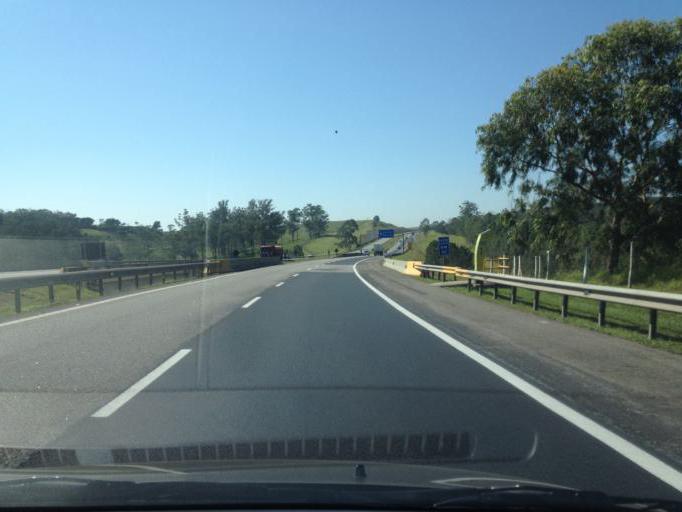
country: BR
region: Sao Paulo
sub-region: Guararema
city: Guararema
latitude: -23.3600
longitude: -46.1235
